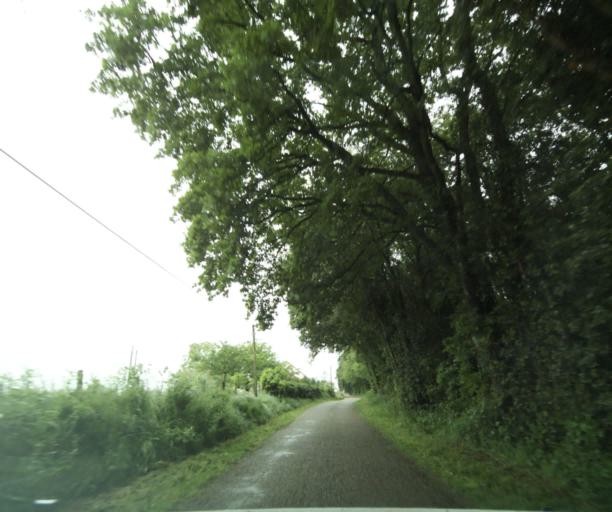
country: FR
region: Bourgogne
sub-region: Departement de Saone-et-Loire
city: Charolles
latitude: 46.4206
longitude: 4.3753
